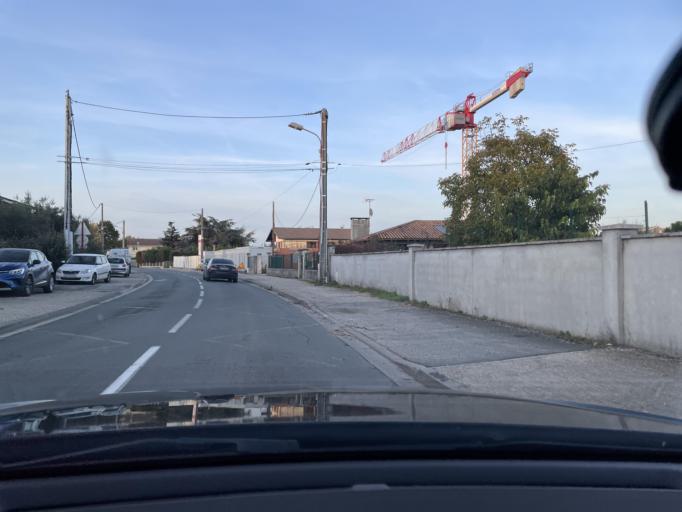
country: FR
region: Aquitaine
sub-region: Departement de la Gironde
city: Villenave-d'Ornon
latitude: 44.7751
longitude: -0.5382
